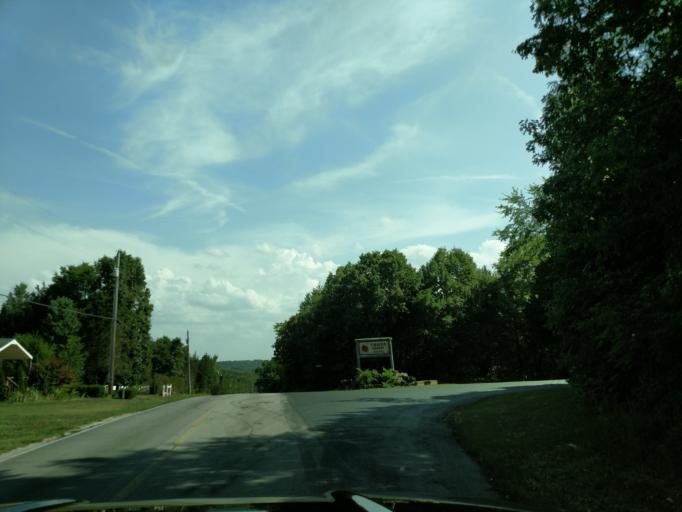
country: US
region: Missouri
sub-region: Barry County
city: Shell Knob
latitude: 36.6041
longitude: -93.5813
